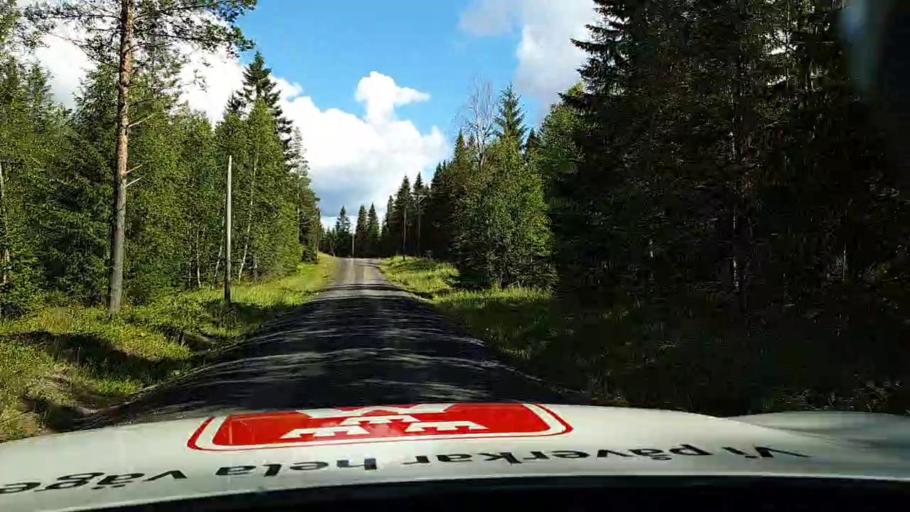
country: SE
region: Jaemtland
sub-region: Krokoms Kommun
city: Valla
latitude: 63.3331
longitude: 13.7222
